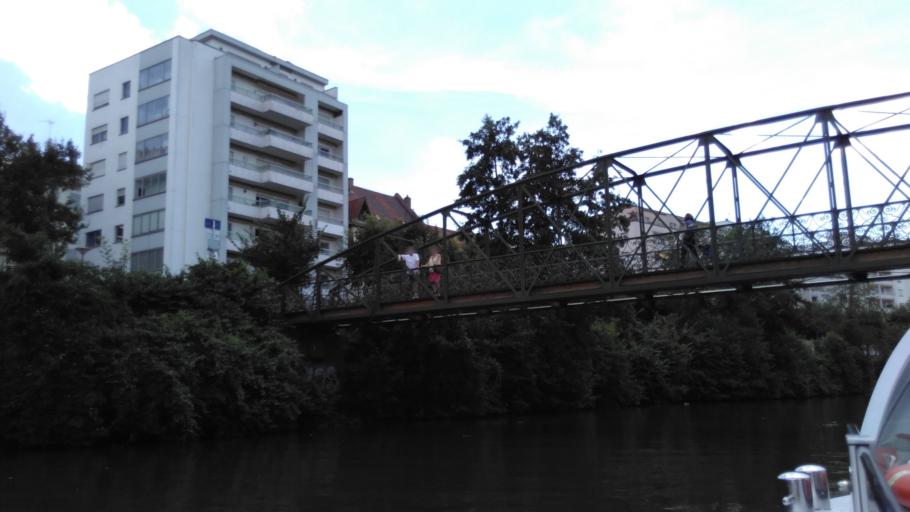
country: FR
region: Alsace
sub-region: Departement du Bas-Rhin
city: Schiltigheim
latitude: 48.5928
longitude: 7.7666
